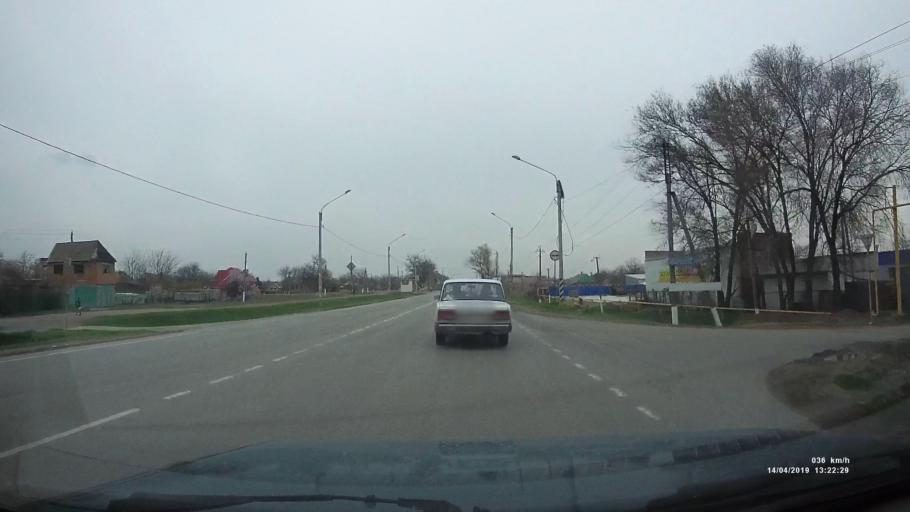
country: RU
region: Rostov
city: Kuleshovka
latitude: 47.0827
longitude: 39.5100
